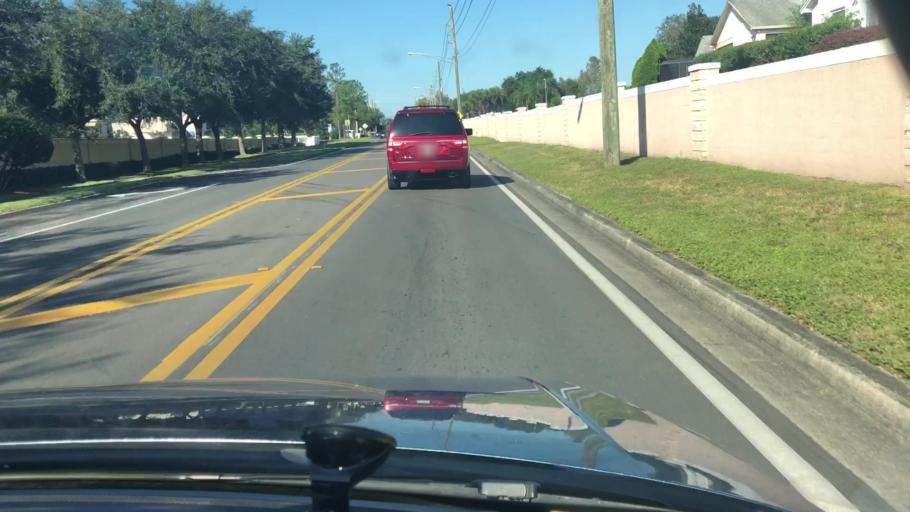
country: US
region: Florida
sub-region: Polk County
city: Gibsonia
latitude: 28.1140
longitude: -81.9431
